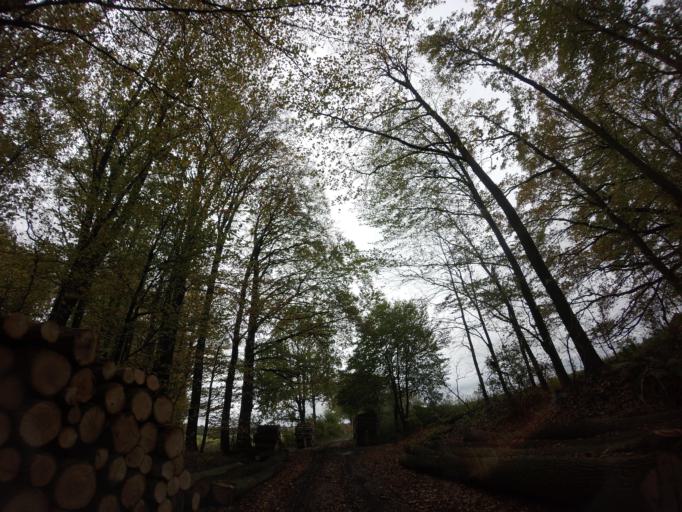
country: PL
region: West Pomeranian Voivodeship
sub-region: Powiat choszczenski
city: Krzecin
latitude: 53.0095
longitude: 15.4578
